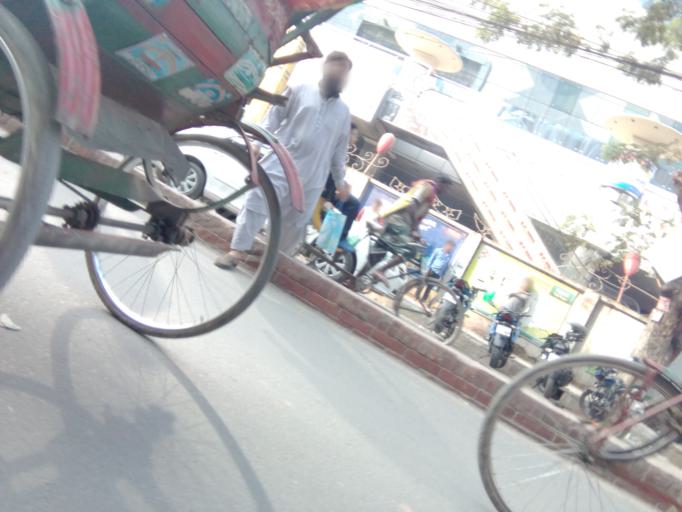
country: BD
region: Dhaka
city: Paltan
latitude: 23.8126
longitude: 90.4240
